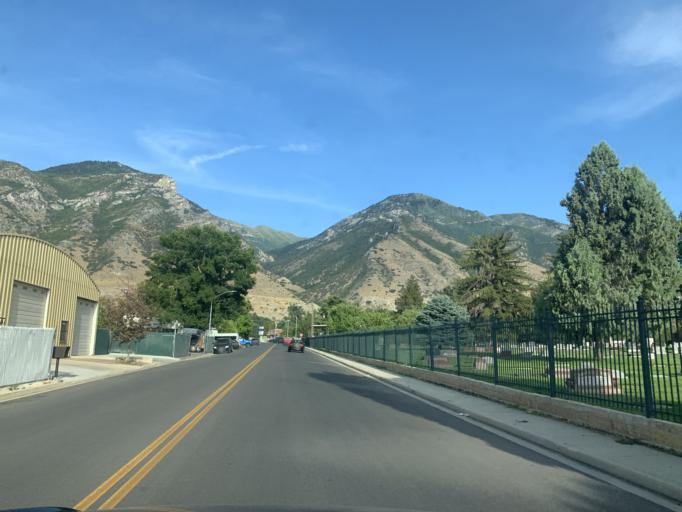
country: US
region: Utah
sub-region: Utah County
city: Provo
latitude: 40.2261
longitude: -111.6457
